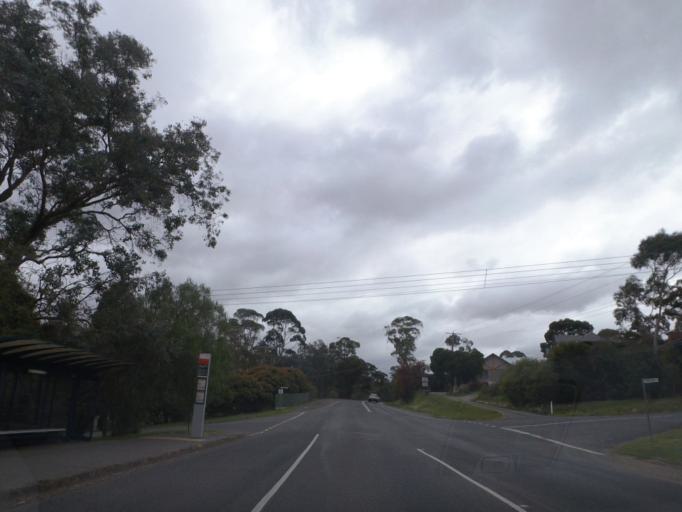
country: AU
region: Victoria
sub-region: Nillumbik
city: North Warrandyte
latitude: -37.7436
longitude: 145.2107
